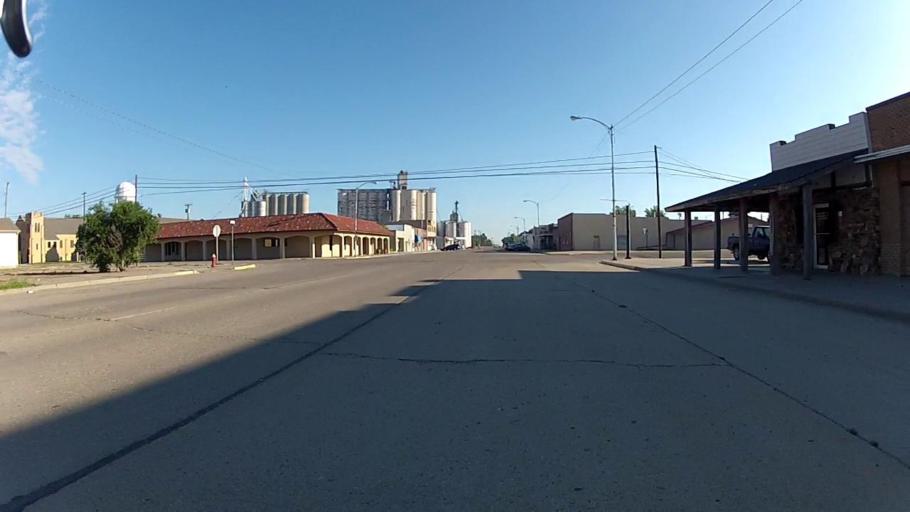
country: US
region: Kansas
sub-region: Haskell County
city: Sublette
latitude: 37.4809
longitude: -100.8436
